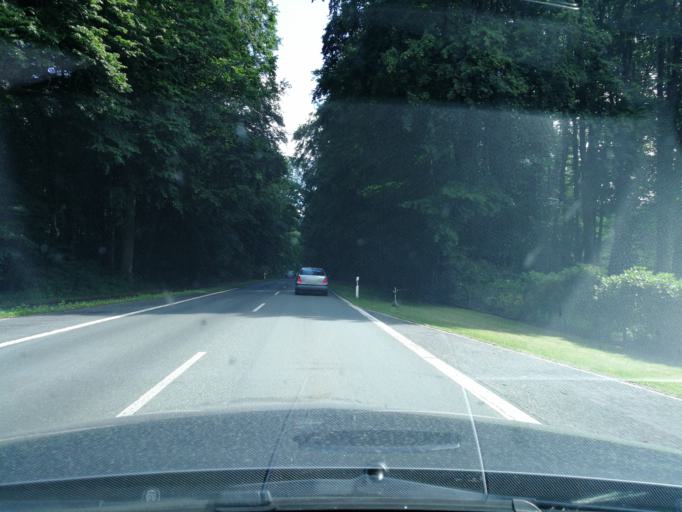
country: DE
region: North Rhine-Westphalia
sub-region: Regierungsbezirk Dusseldorf
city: Kleve
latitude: 51.7416
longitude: 6.0824
